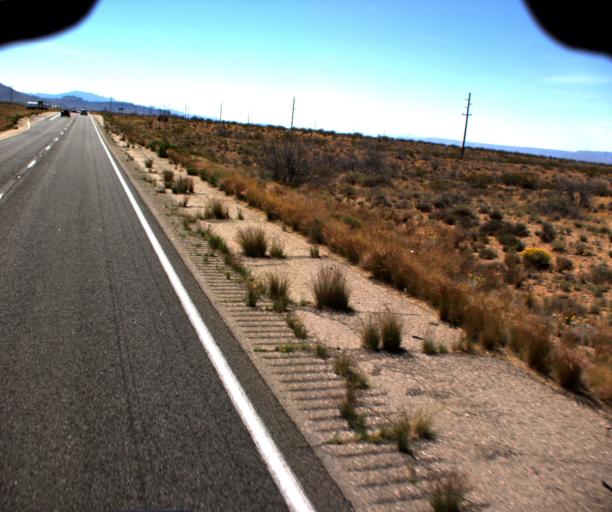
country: US
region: Arizona
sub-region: Mohave County
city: Golden Valley
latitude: 35.3248
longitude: -114.2075
